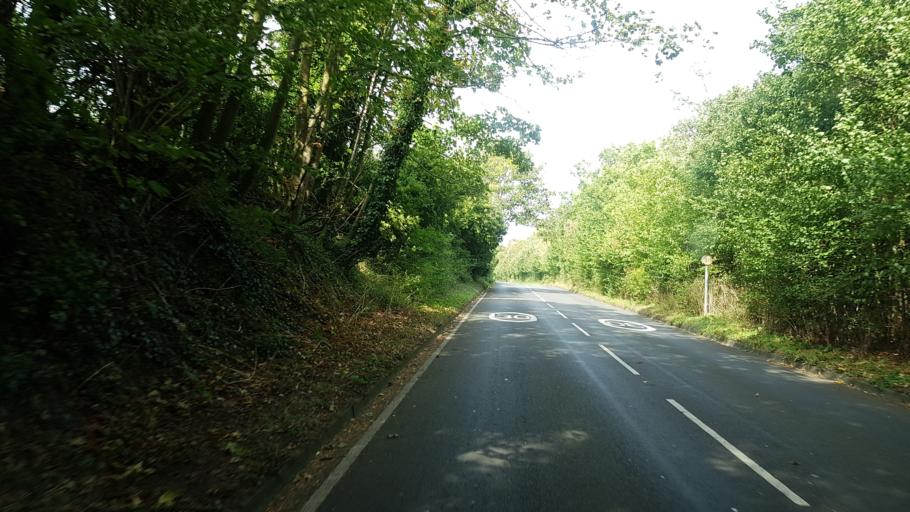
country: GB
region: England
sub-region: Kent
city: Larkfield
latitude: 51.2920
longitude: 0.4291
